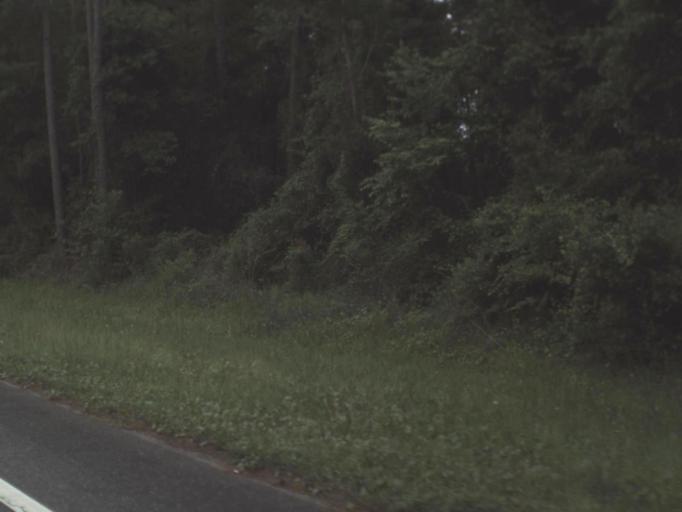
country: US
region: Florida
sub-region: Columbia County
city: Watertown
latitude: 30.1030
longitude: -82.4844
